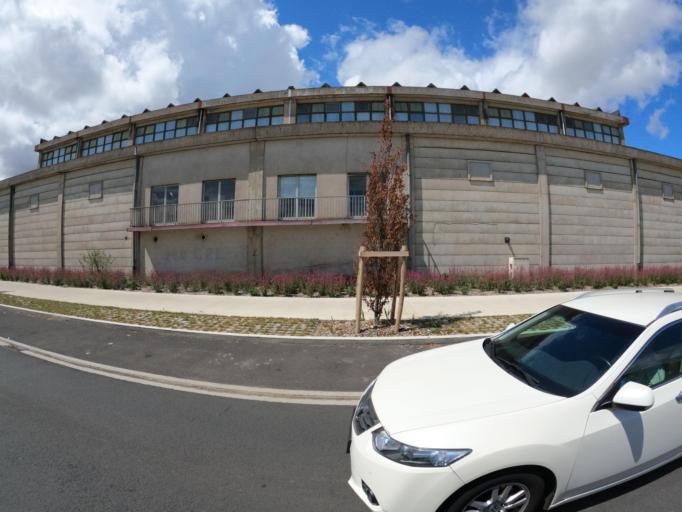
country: FR
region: Pays de la Loire
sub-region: Departement de Maine-et-Loire
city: Avrille
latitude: 47.5235
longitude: -0.6109
